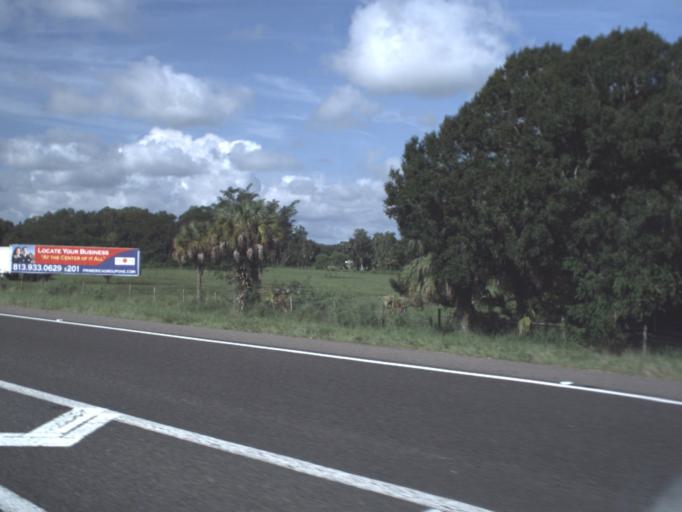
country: US
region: Florida
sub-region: Manatee County
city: Ellenton
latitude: 27.5976
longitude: -82.5066
